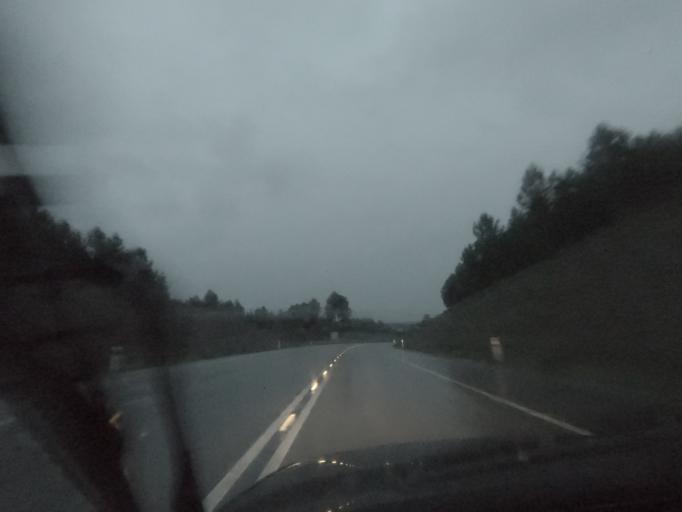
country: PT
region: Vila Real
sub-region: Vila Real
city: Vila Real
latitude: 41.2700
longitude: -7.6804
